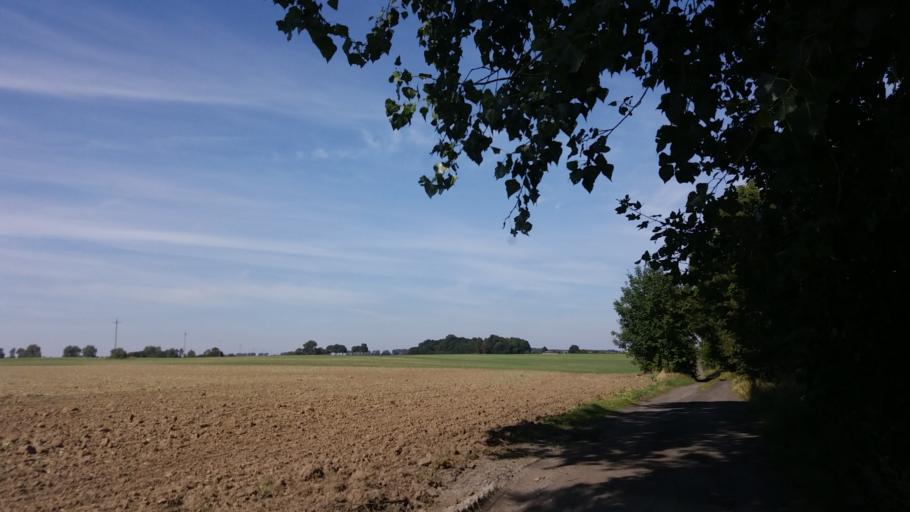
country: PL
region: West Pomeranian Voivodeship
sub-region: Powiat choszczenski
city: Choszczno
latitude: 53.1303
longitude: 15.4058
